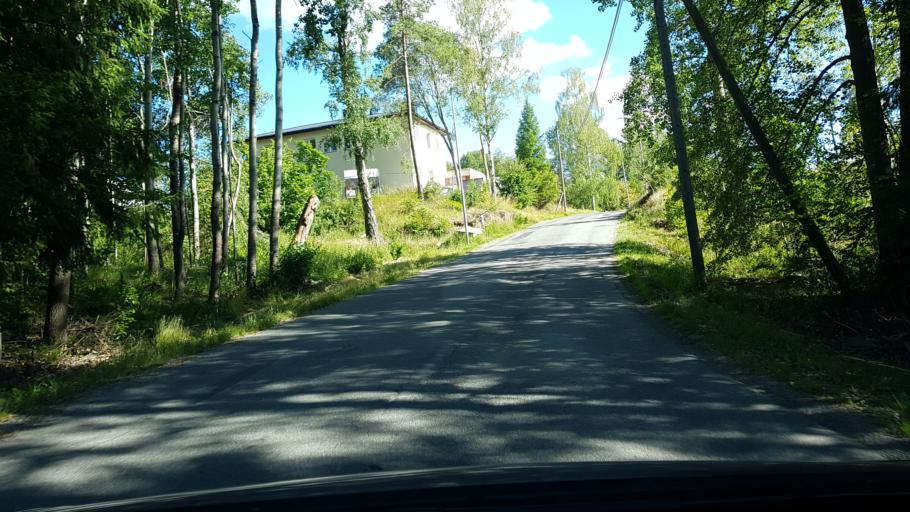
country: SE
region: Stockholm
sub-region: Upplands-Bro Kommun
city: Kungsaengen
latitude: 59.4813
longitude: 17.8002
